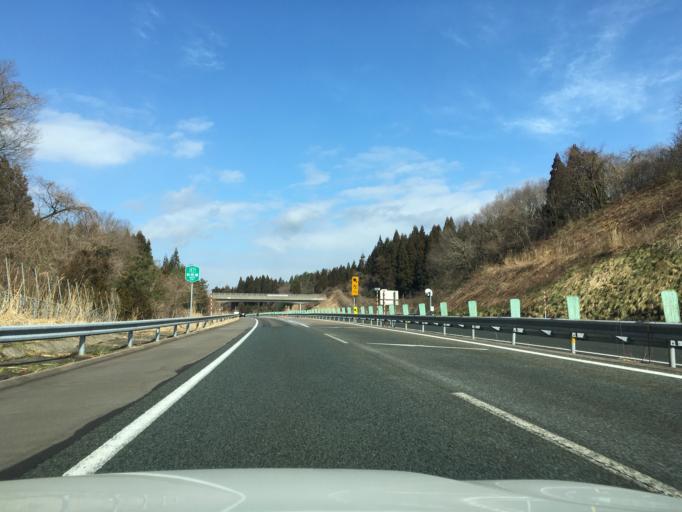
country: JP
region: Akita
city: Akita
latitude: 39.7271
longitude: 140.1805
